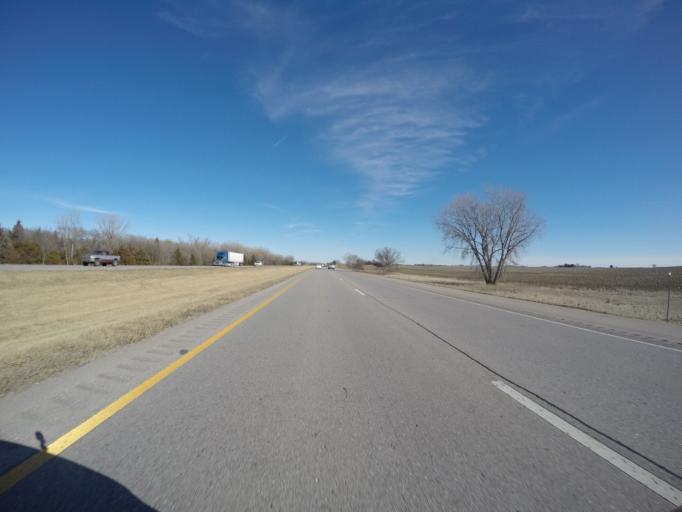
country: US
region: Nebraska
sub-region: Seward County
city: Milford
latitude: 40.8202
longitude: -96.8853
